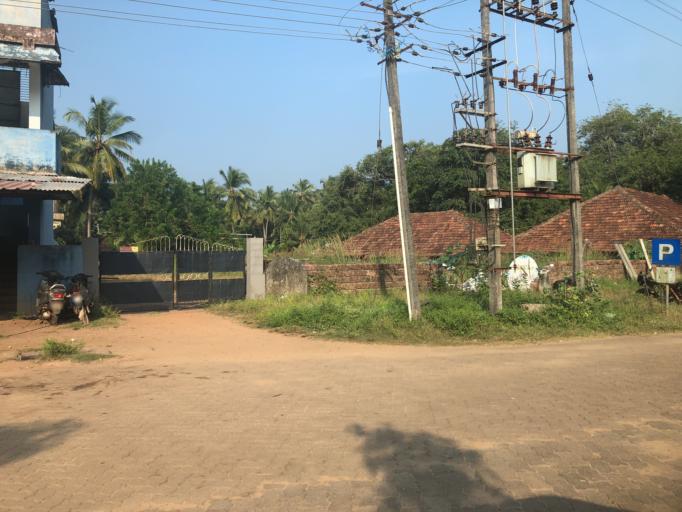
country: IN
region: Karnataka
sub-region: Dakshina Kannada
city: Ullal
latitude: 12.8204
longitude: 74.8445
